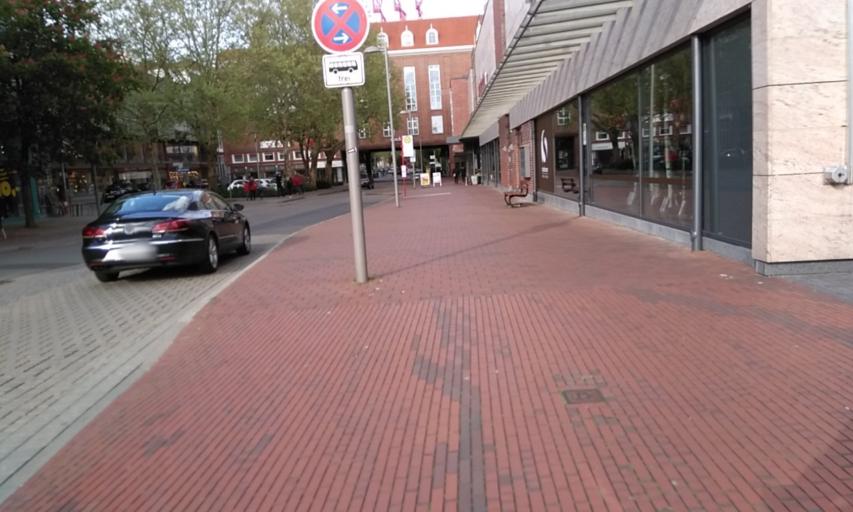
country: DE
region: Lower Saxony
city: Buxtehude
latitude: 53.4744
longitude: 9.6983
